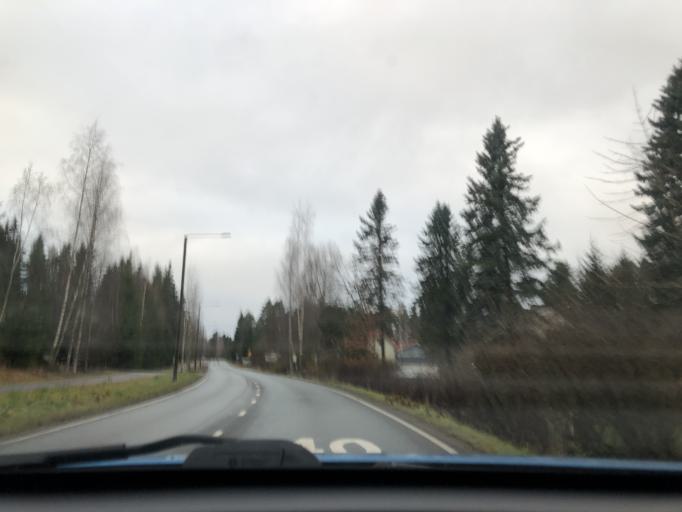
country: FI
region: Pirkanmaa
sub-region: Tampere
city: Kangasala
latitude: 61.5257
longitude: 24.0276
